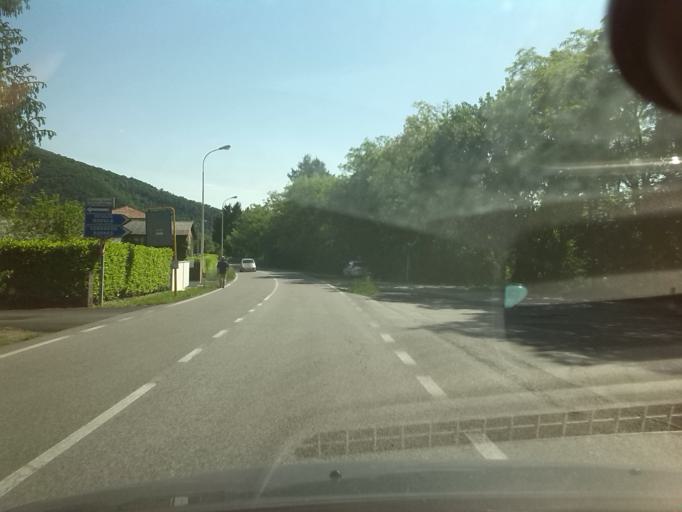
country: IT
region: Friuli Venezia Giulia
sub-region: Provincia di Udine
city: San Pietro al Natisone
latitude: 46.1224
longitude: 13.4823
